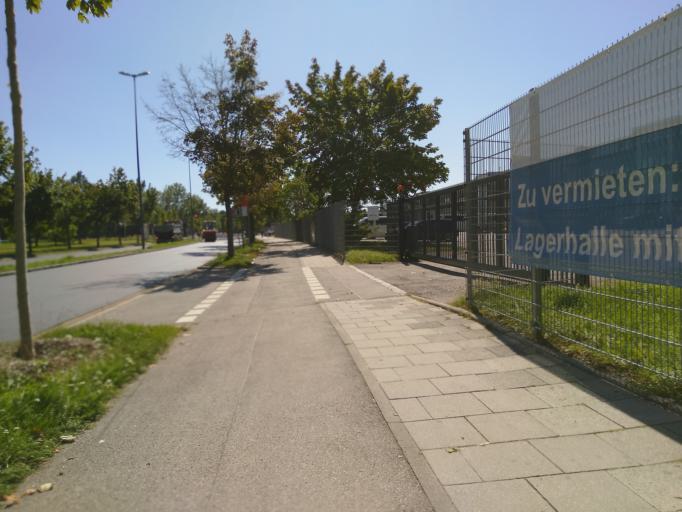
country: DE
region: Bavaria
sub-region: Upper Bavaria
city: Unterfoehring
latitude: 48.2003
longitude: 11.6056
